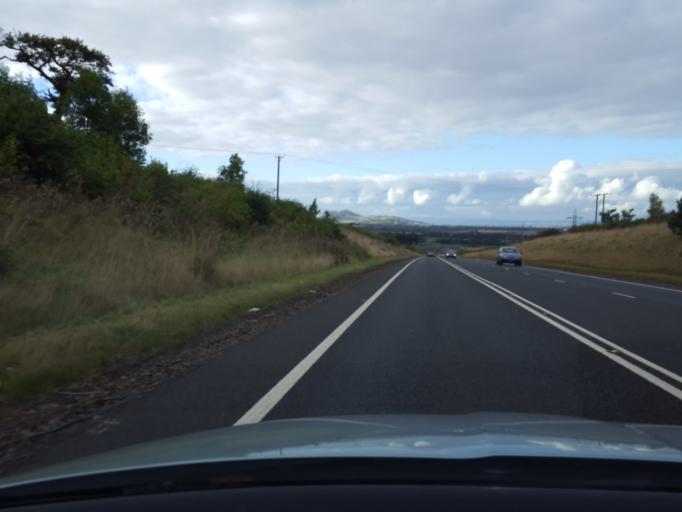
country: GB
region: Scotland
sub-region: Midlothian
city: Dalkeith
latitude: 55.9035
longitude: -3.0300
